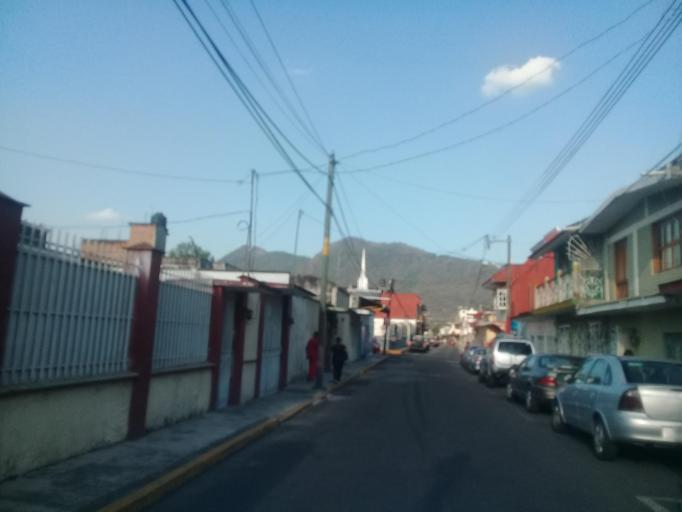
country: MX
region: Veracruz
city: Orizaba
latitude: 18.8566
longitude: -97.1100
